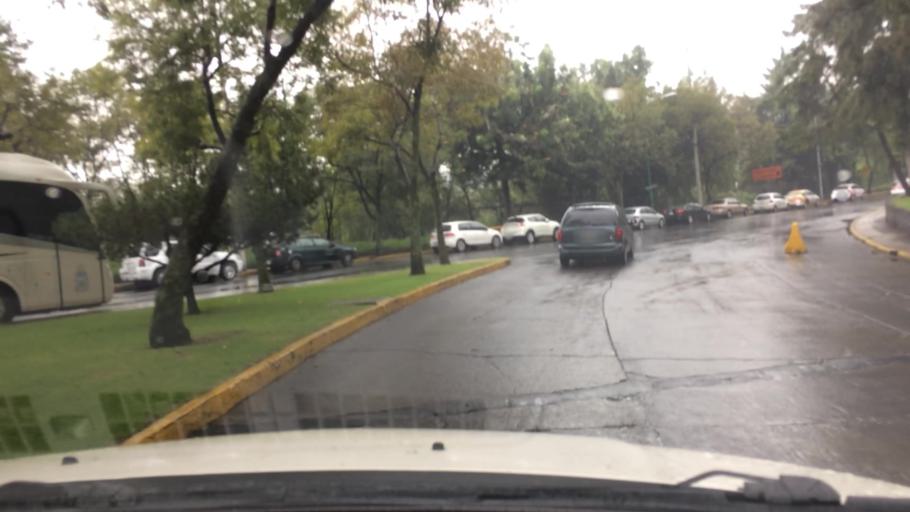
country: MX
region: Mexico City
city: Magdalena Contreras
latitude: 19.3352
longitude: -99.1932
